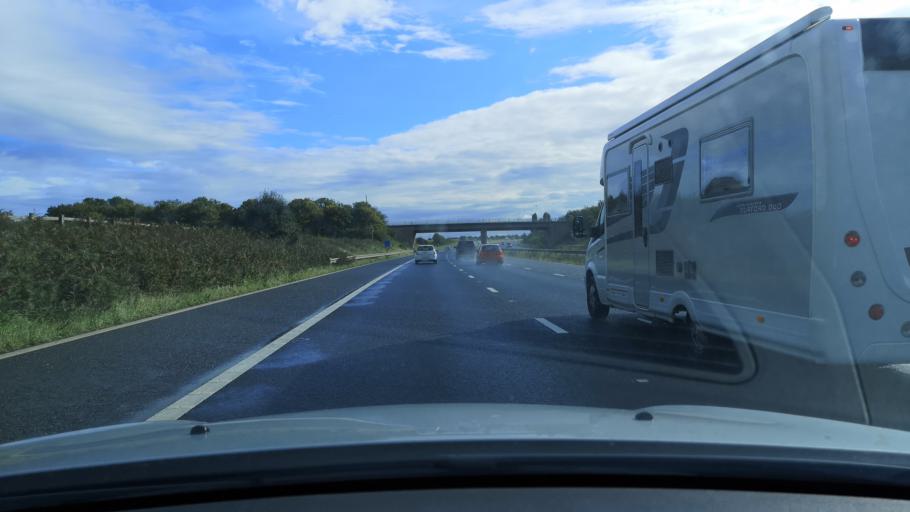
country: GB
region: England
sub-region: East Riding of Yorkshire
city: Pollington
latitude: 53.6940
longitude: -1.1224
